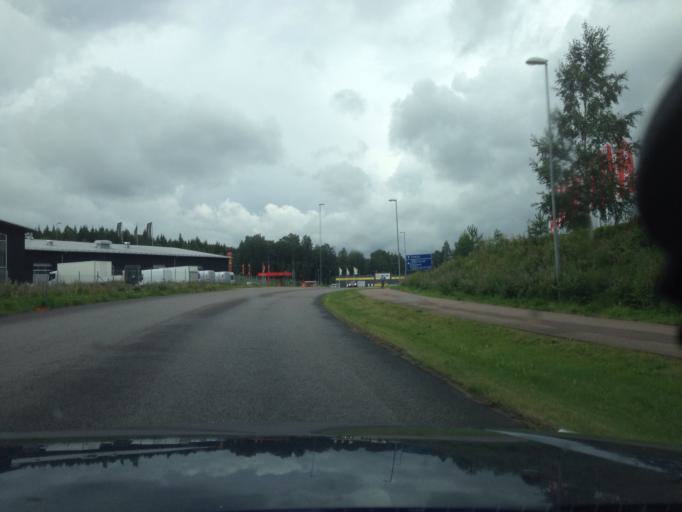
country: SE
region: Dalarna
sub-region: Ludvika Kommun
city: Ludvika
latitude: 60.1350
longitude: 15.1575
